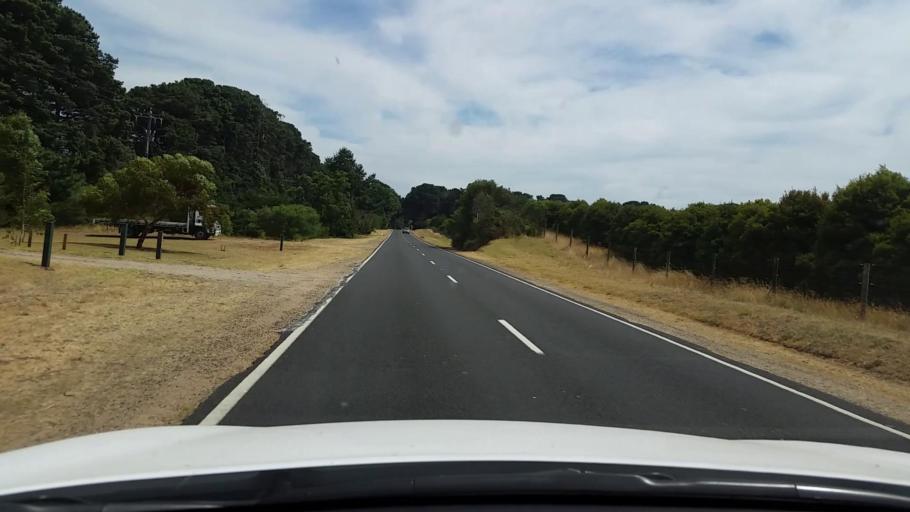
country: AU
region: Victoria
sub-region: Mornington Peninsula
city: Saint Andrews Beach
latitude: -38.4633
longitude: 144.9096
